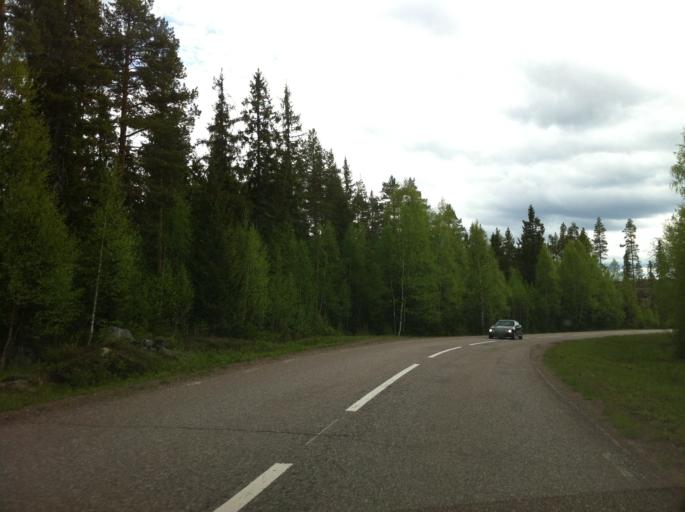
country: NO
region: Hedmark
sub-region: Trysil
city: Innbygda
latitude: 61.3474
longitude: 13.0641
